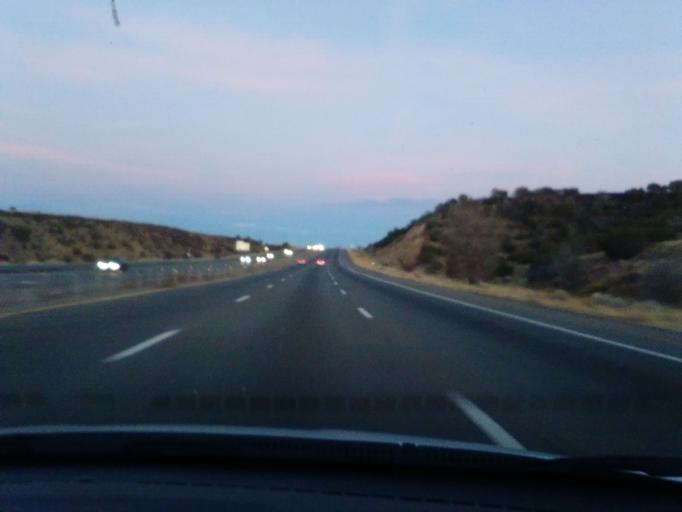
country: US
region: New Mexico
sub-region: Santa Fe County
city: La Cienega
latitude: 35.5211
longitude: -106.2074
